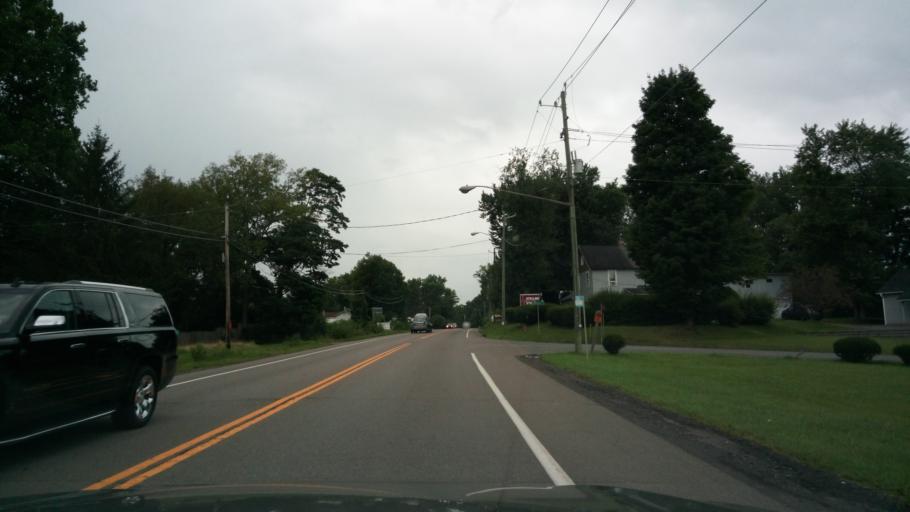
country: US
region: New York
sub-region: Tompkins County
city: South Hill
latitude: 42.4087
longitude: -76.5413
